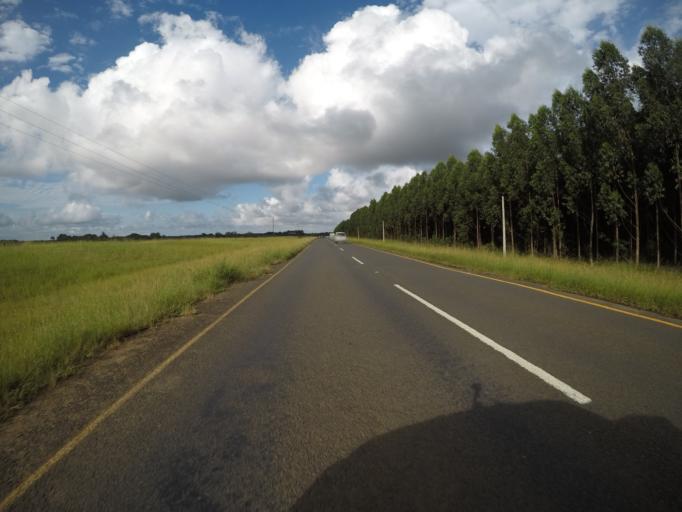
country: ZA
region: KwaZulu-Natal
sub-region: uMkhanyakude District Municipality
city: Mtubatuba
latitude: -28.3835
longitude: 32.2406
